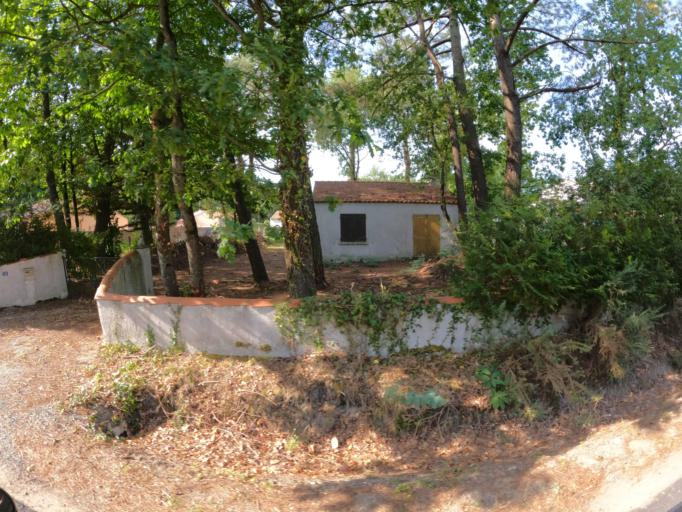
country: FR
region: Pays de la Loire
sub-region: Departement de la Vendee
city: Soullans
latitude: 46.8049
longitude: -1.8785
